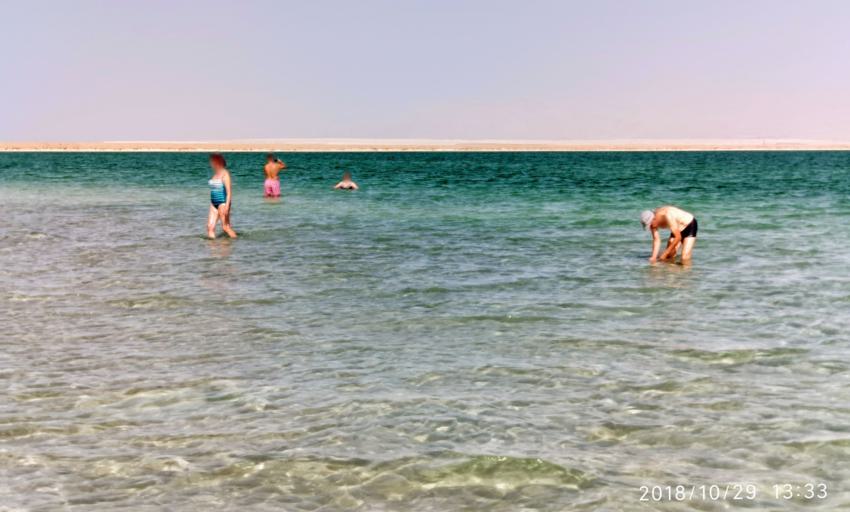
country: IL
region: Southern District
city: `En Boqeq
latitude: 31.1740
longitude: 35.3695
